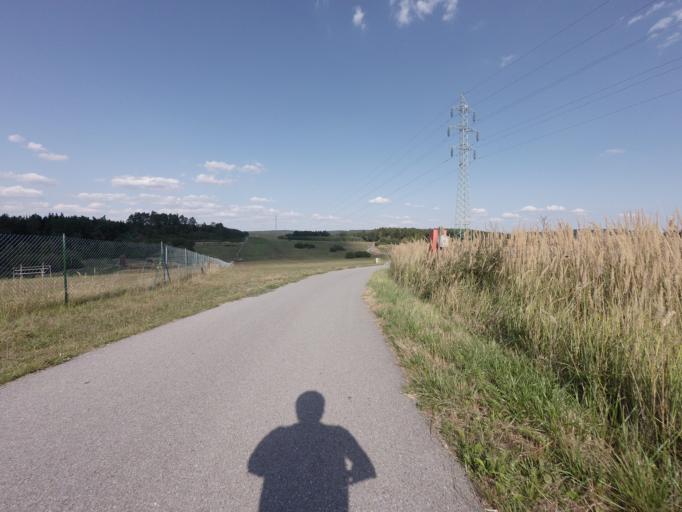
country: CZ
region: Jihocesky
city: Tyn nad Vltavou
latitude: 49.1738
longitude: 14.4334
